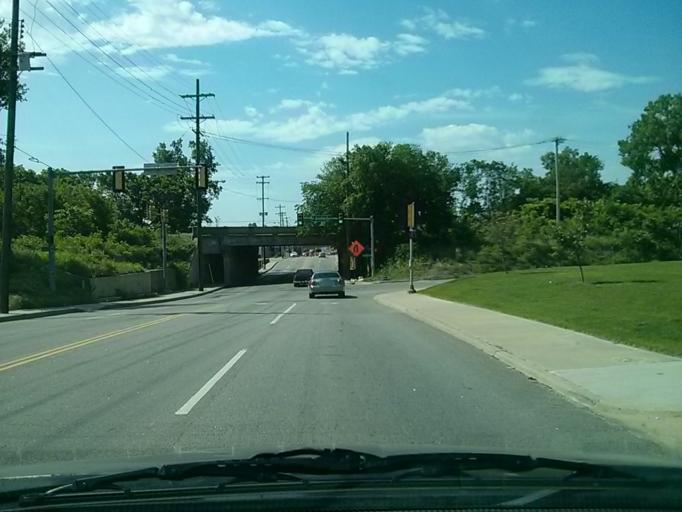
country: US
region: Oklahoma
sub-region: Tulsa County
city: Tulsa
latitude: 36.1629
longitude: -95.9757
